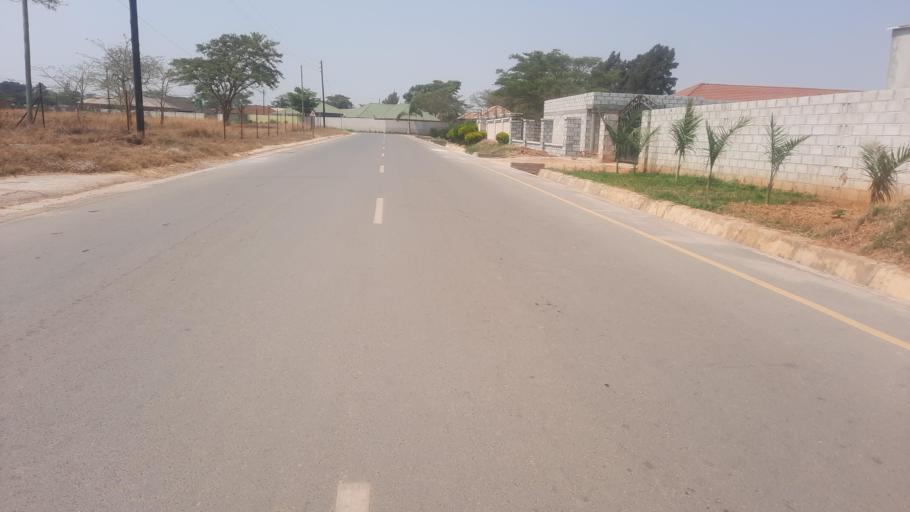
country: ZM
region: Lusaka
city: Lusaka
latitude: -15.3922
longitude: 28.3929
